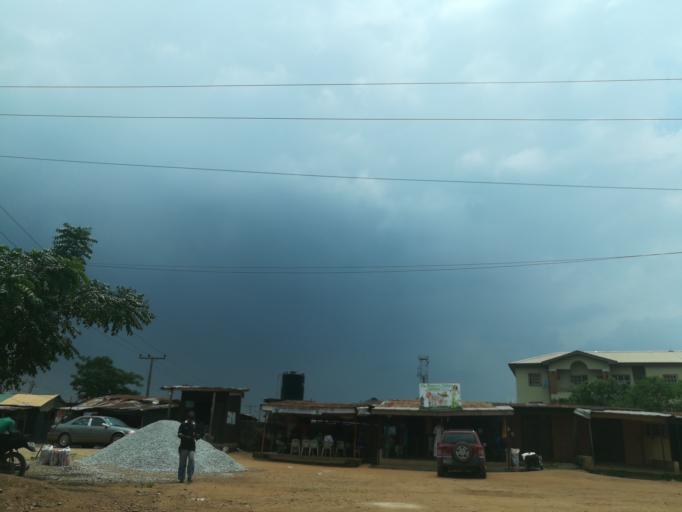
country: NG
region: Lagos
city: Ikorodu
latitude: 6.6134
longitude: 3.5758
